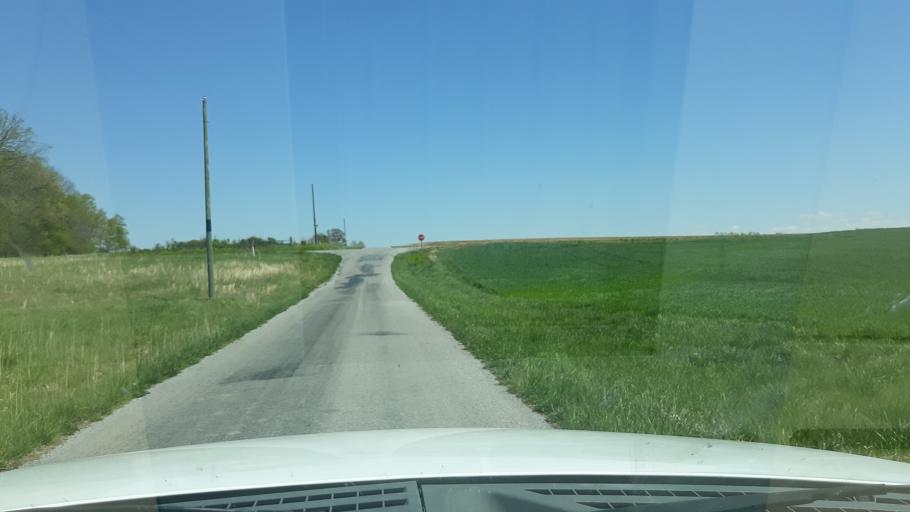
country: US
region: Illinois
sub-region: Saline County
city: Harrisburg
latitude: 37.8849
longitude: -88.6525
